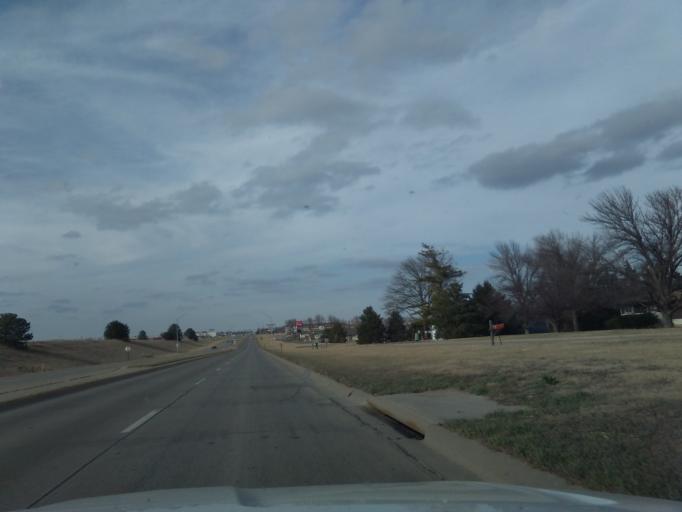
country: US
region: Nebraska
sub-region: Gage County
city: Beatrice
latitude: 40.2947
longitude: -96.7467
